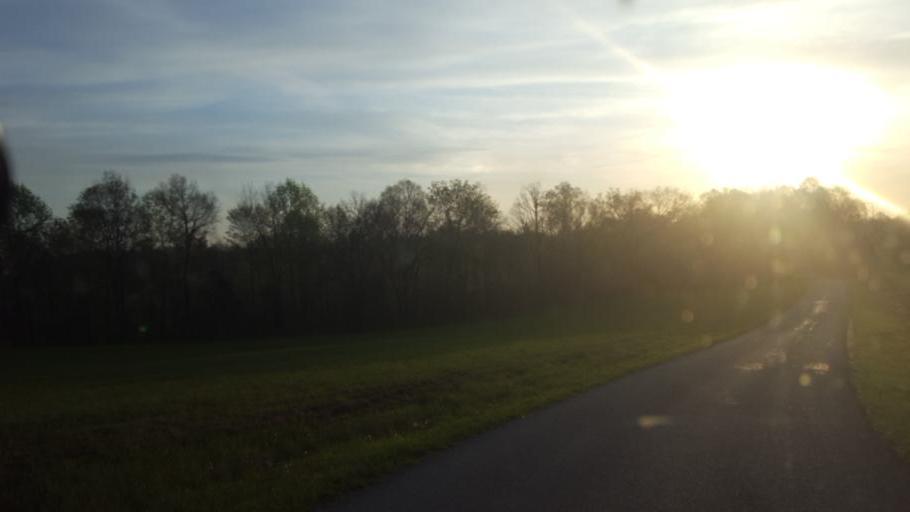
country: US
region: Kentucky
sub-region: Barren County
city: Cave City
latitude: 37.1698
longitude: -86.0072
